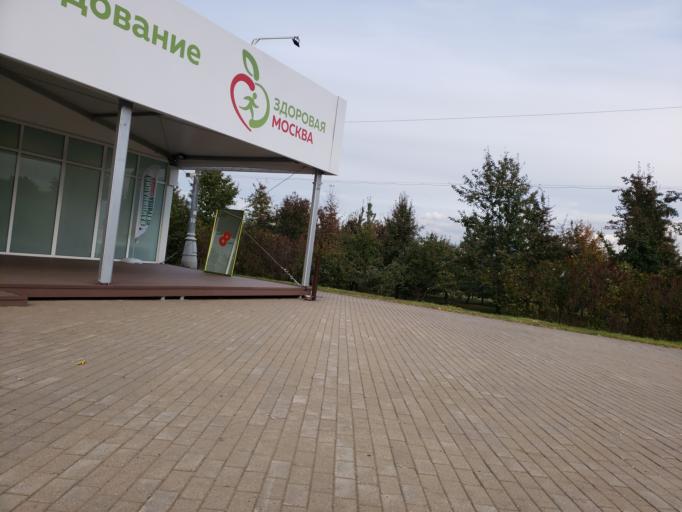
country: RU
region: Moscow
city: Kolomenskoye
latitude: 55.6728
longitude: 37.6724
